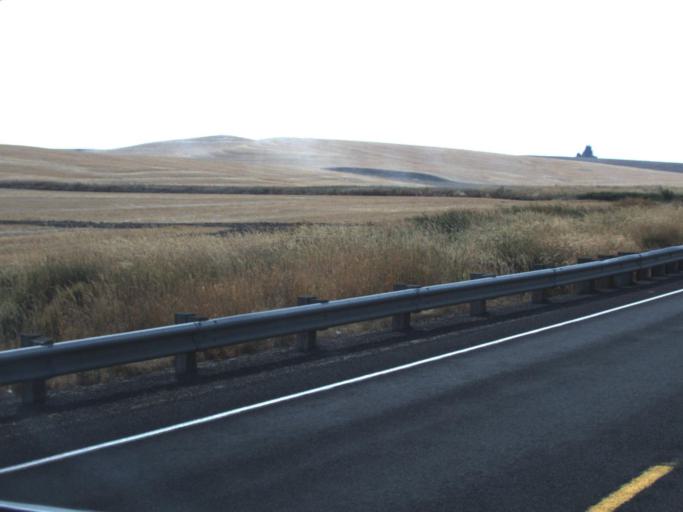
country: US
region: Washington
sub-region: Whitman County
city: Pullman
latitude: 46.8788
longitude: -117.1265
